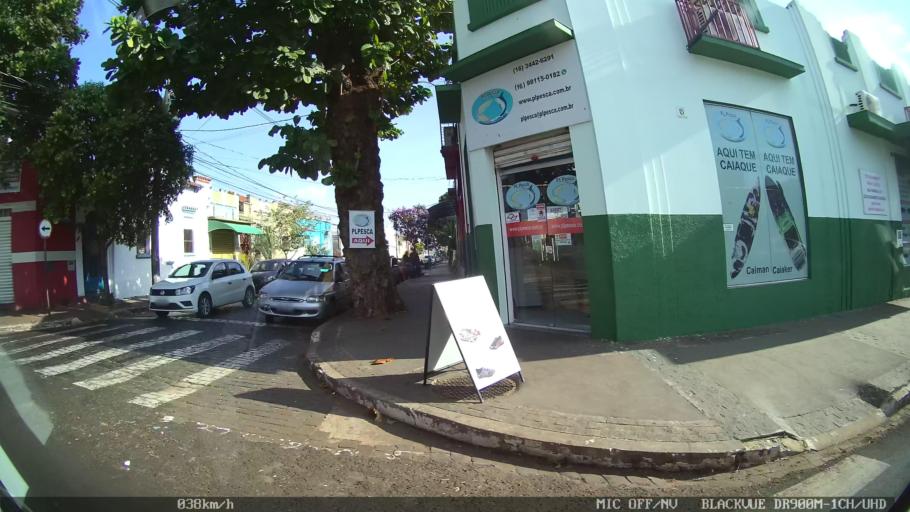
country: BR
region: Sao Paulo
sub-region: Ribeirao Preto
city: Ribeirao Preto
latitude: -21.1662
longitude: -47.8064
